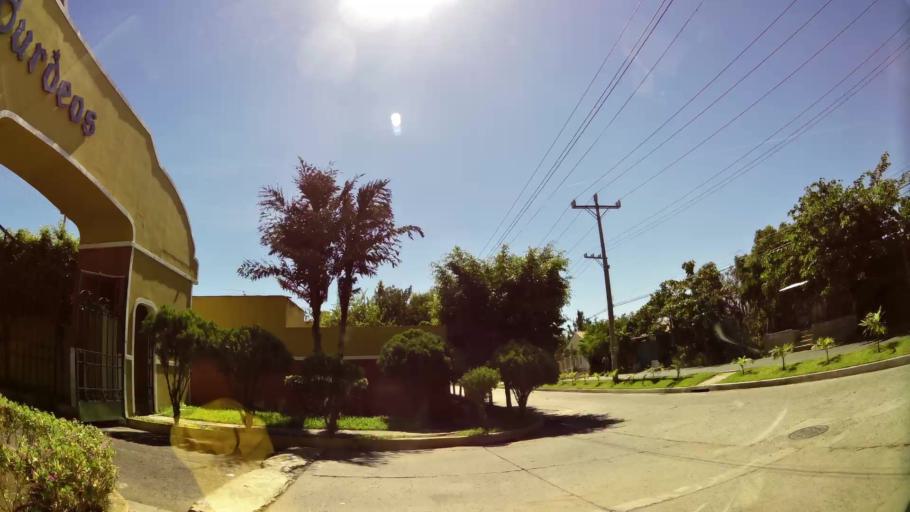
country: SV
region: La Libertad
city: San Juan Opico
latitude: 13.7956
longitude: -89.3600
